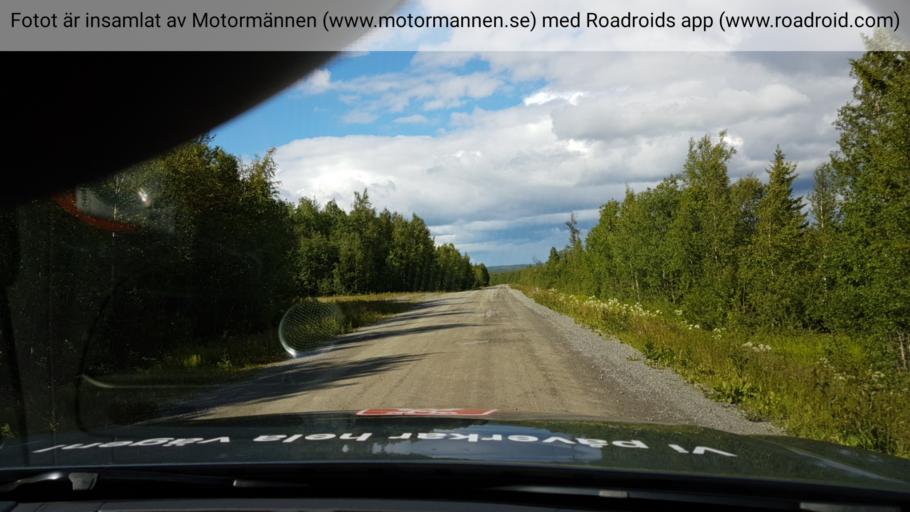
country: SE
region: Jaemtland
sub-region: Krokoms Kommun
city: Valla
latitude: 63.0521
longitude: 13.9637
